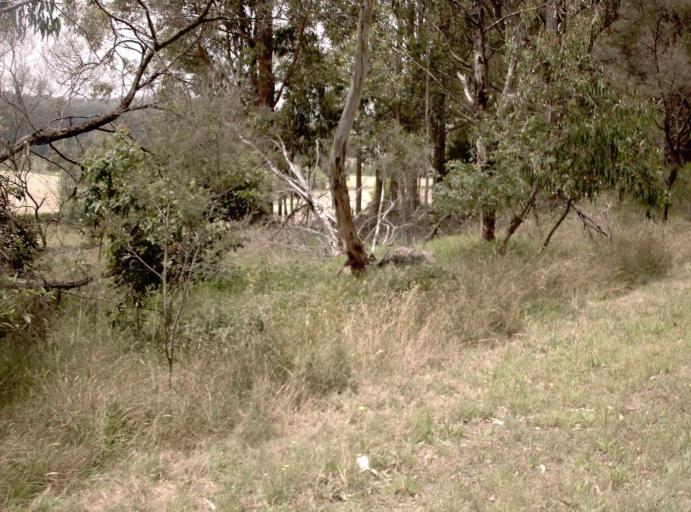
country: AU
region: Victoria
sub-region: Latrobe
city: Traralgon
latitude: -38.4410
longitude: 146.7323
